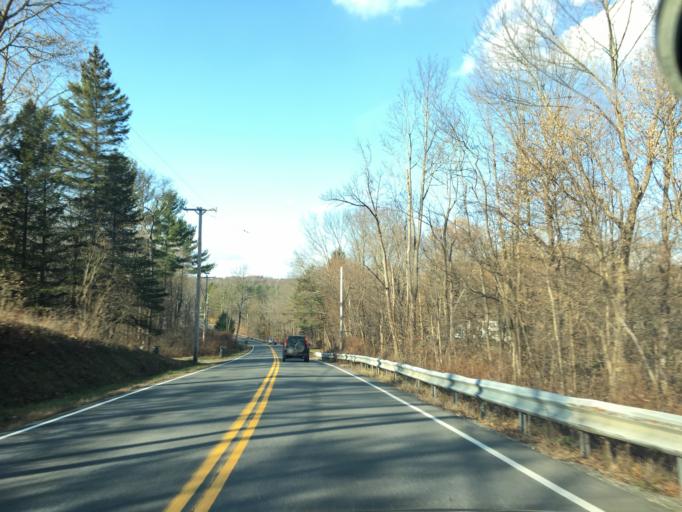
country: US
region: New York
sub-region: Rensselaer County
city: West Sand Lake
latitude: 42.6295
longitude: -73.6610
